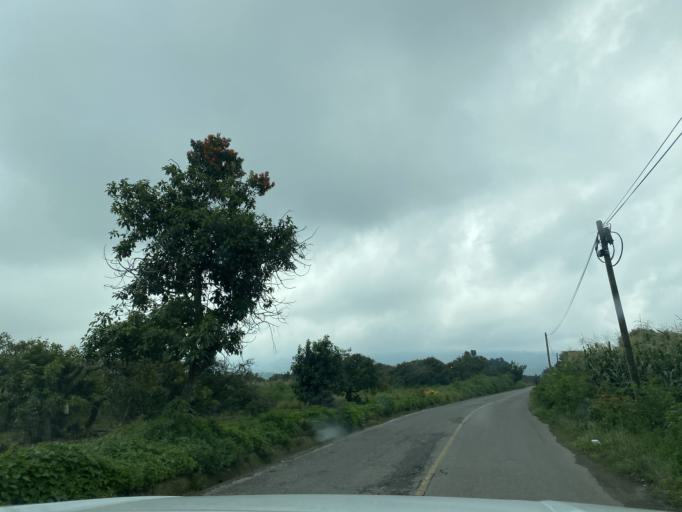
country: MX
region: Morelos
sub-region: Yecapixtla
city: Texcala
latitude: 18.9357
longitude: -98.8125
